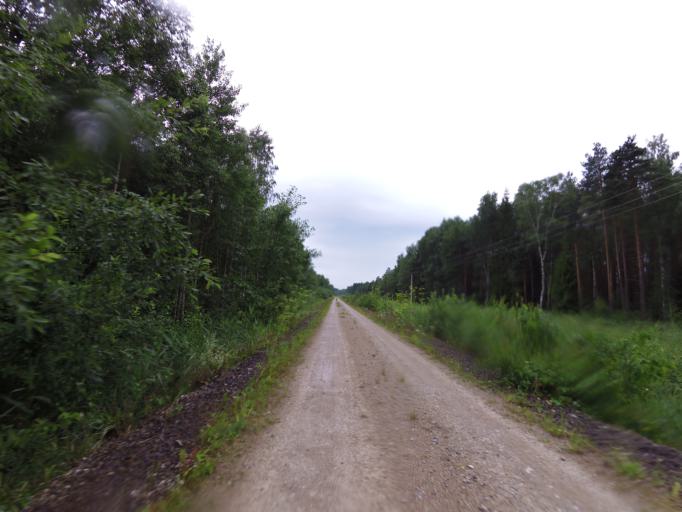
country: EE
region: Harju
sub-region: Nissi vald
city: Turba
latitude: 58.9902
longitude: 23.9974
